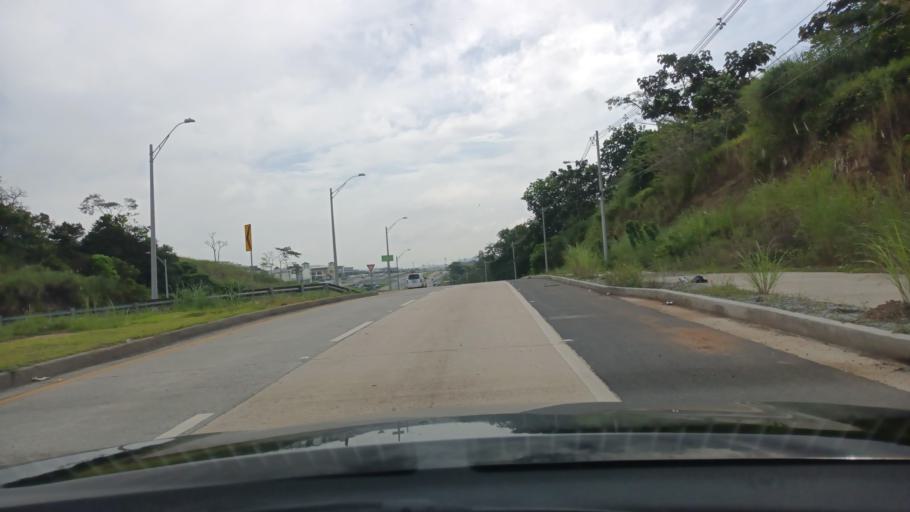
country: PA
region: Panama
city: Las Cumbres
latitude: 9.1038
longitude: -79.5268
